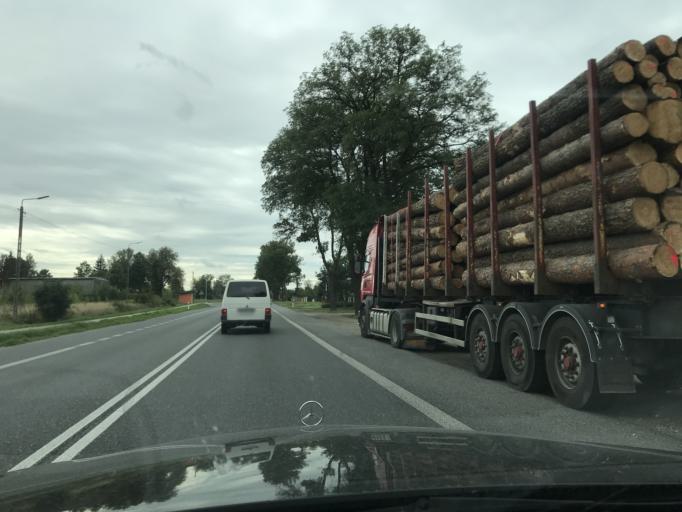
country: PL
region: Lublin Voivodeship
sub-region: Powiat lubelski
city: Niedrzwica Duza
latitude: 51.1030
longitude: 22.3734
